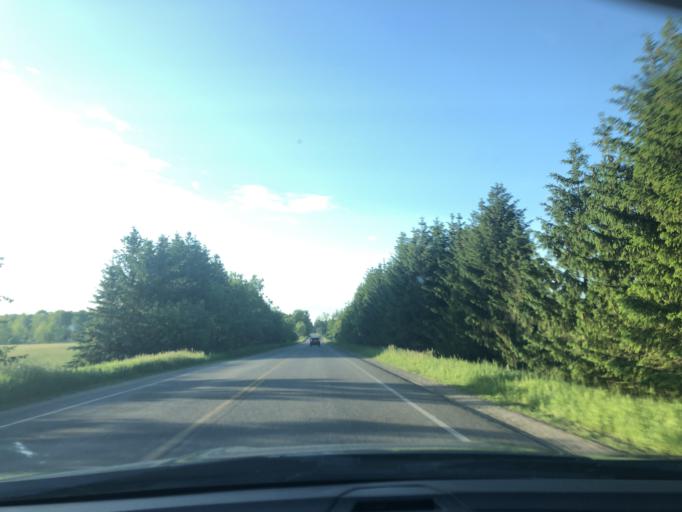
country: US
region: Michigan
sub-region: Missaukee County
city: Lake City
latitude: 44.4312
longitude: -85.0751
